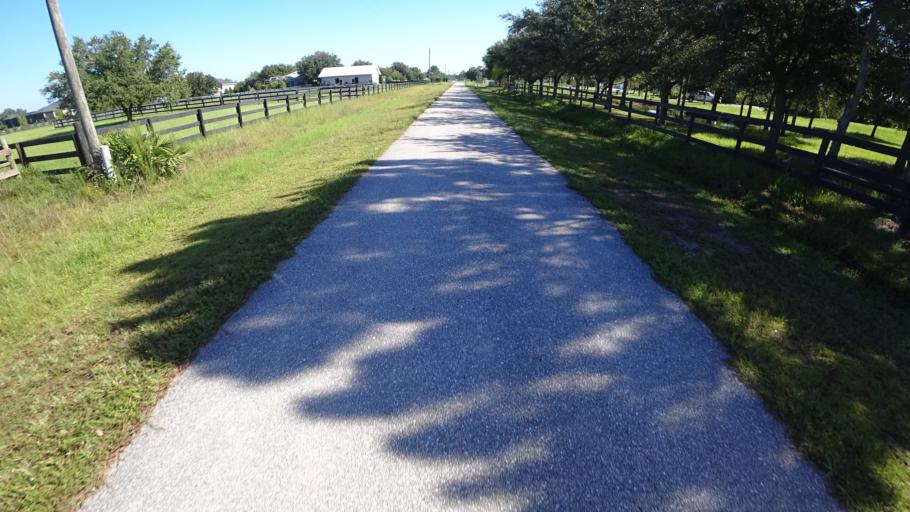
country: US
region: Florida
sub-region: Sarasota County
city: The Meadows
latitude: 27.4146
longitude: -82.3079
